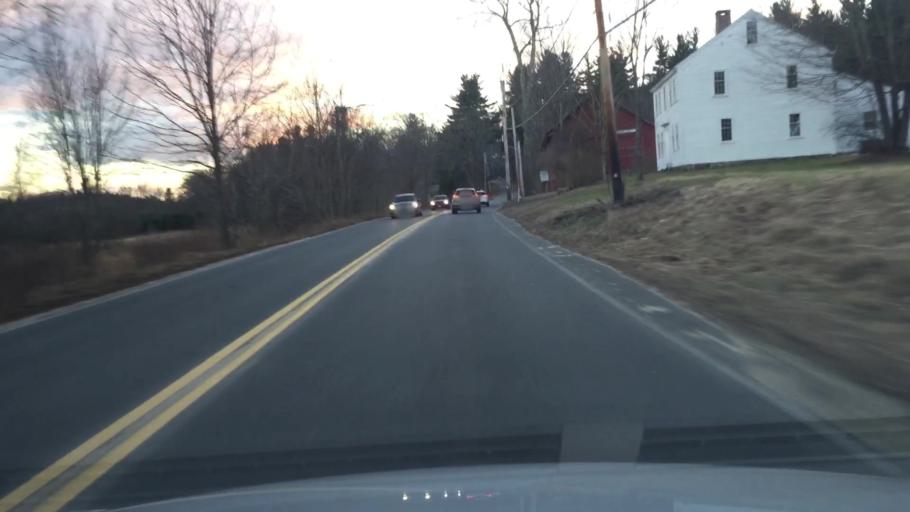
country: US
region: Massachusetts
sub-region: Worcester County
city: Sterling
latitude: 42.4324
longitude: -71.8120
